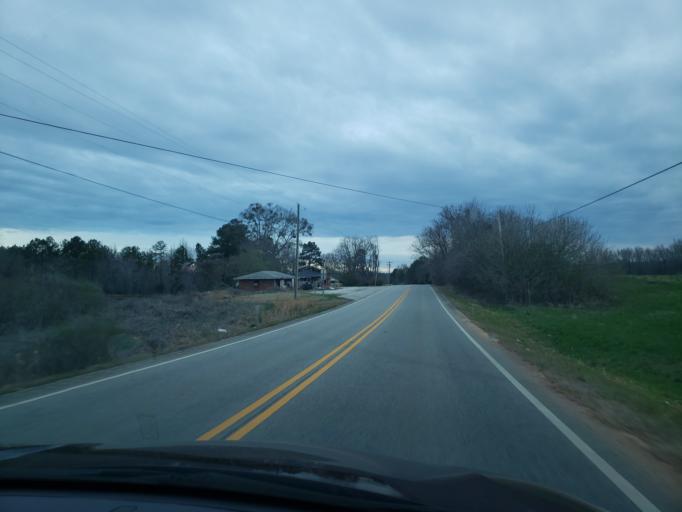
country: US
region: Alabama
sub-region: Chambers County
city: Lafayette
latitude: 32.9590
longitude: -85.4031
